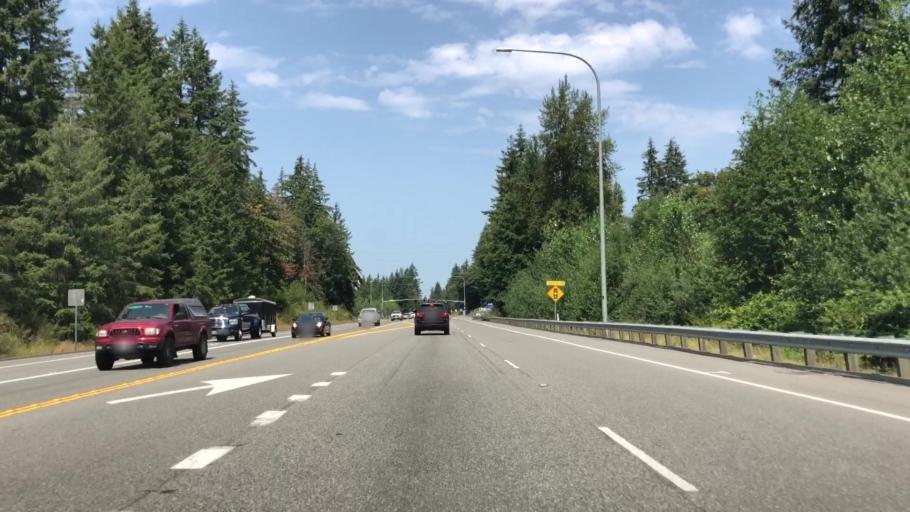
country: US
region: Washington
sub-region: Snohomish County
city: West Lake Stevens
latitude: 47.9754
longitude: -122.1026
